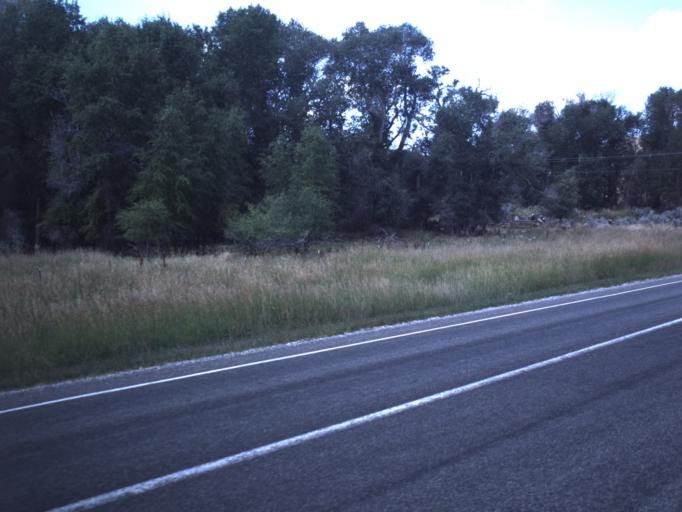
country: US
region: Utah
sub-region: Rich County
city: Randolph
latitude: 41.8558
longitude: -111.3640
